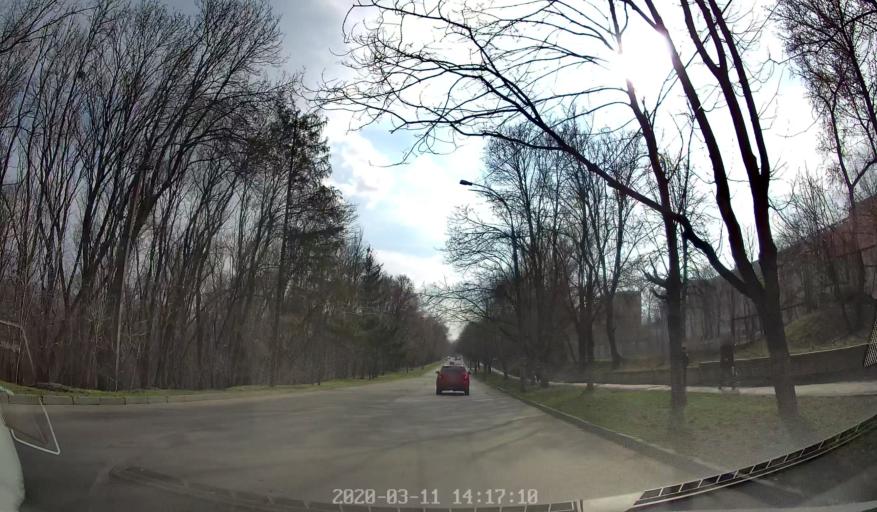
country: MD
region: Chisinau
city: Chisinau
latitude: 47.0475
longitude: 28.8701
